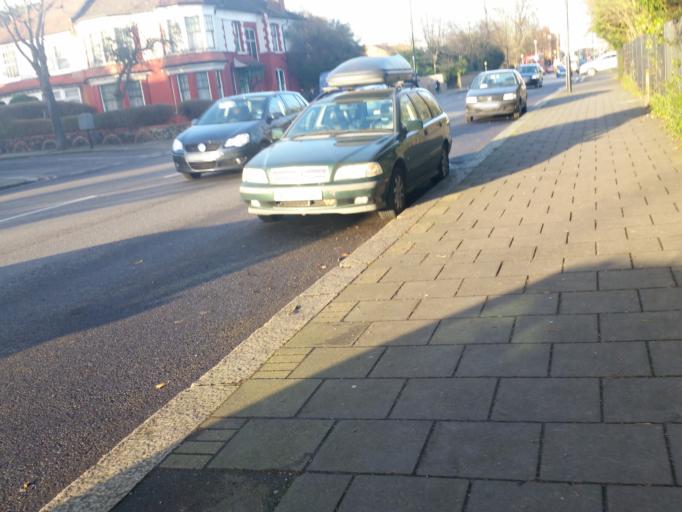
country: GB
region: England
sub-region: Greater London
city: Enfield
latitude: 51.6277
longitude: -0.0983
